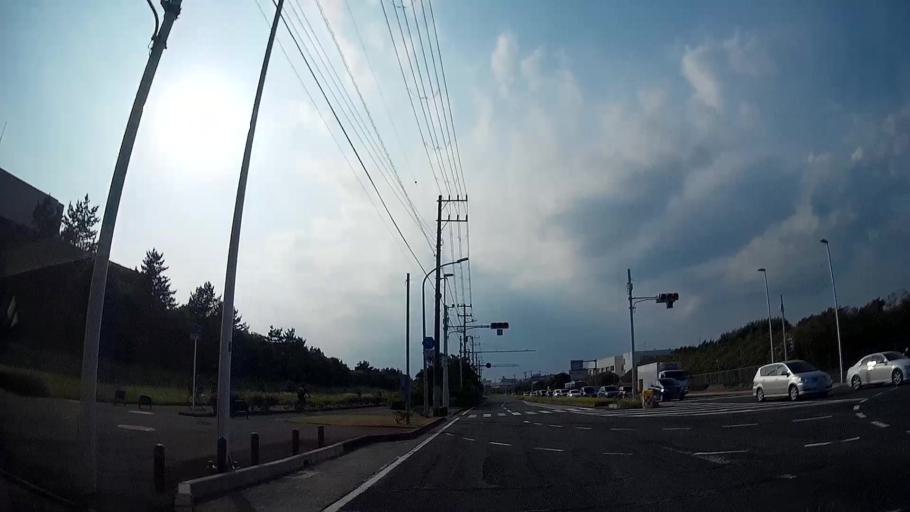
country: JP
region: Chiba
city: Funabashi
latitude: 35.6531
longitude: 140.0245
